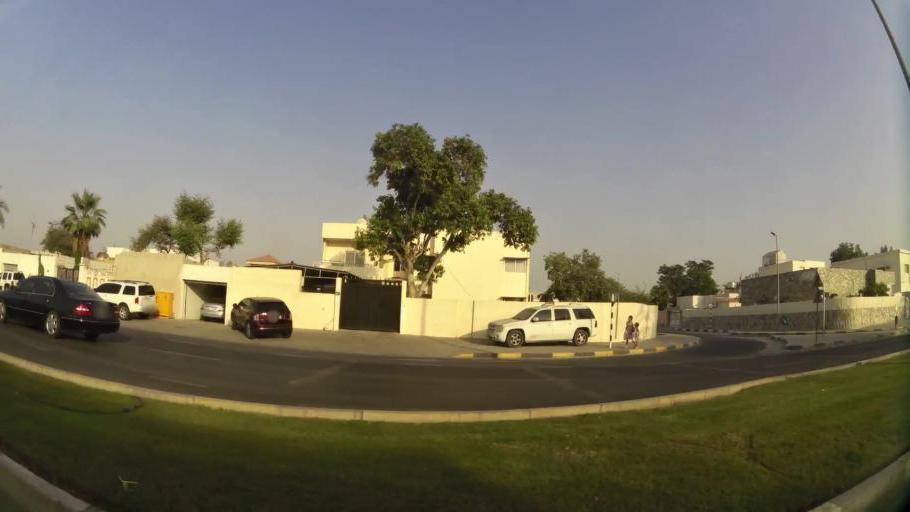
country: AE
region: Ash Shariqah
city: Sharjah
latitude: 25.3699
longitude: 55.4254
